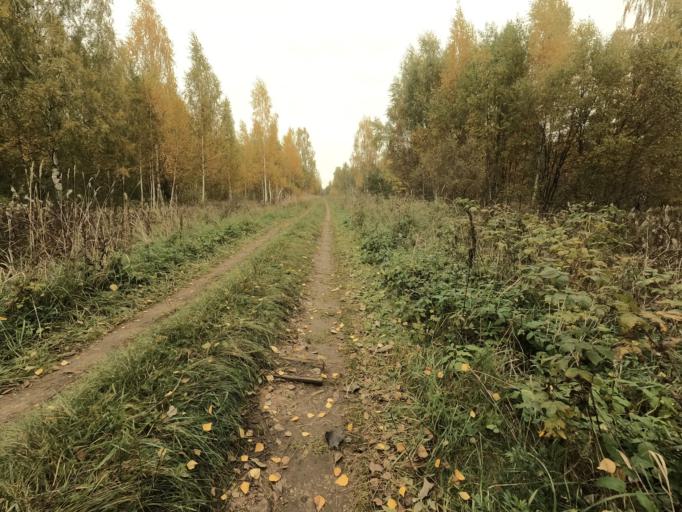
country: RU
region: Novgorod
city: Pankovka
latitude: 58.8663
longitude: 30.9338
